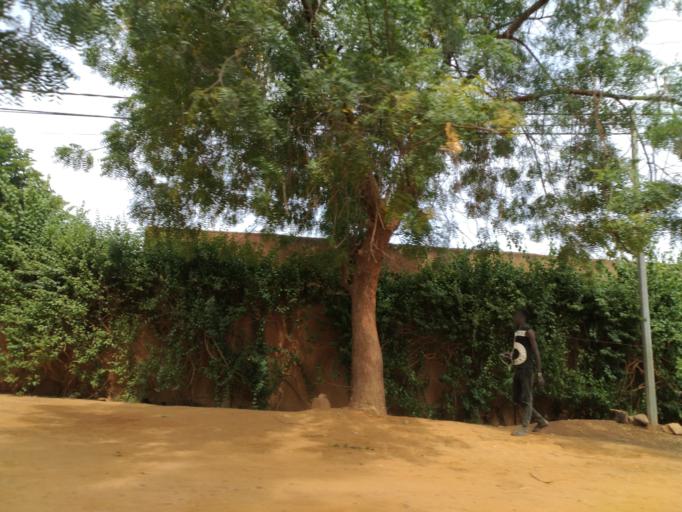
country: NE
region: Niamey
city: Niamey
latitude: 13.5421
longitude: 2.0669
